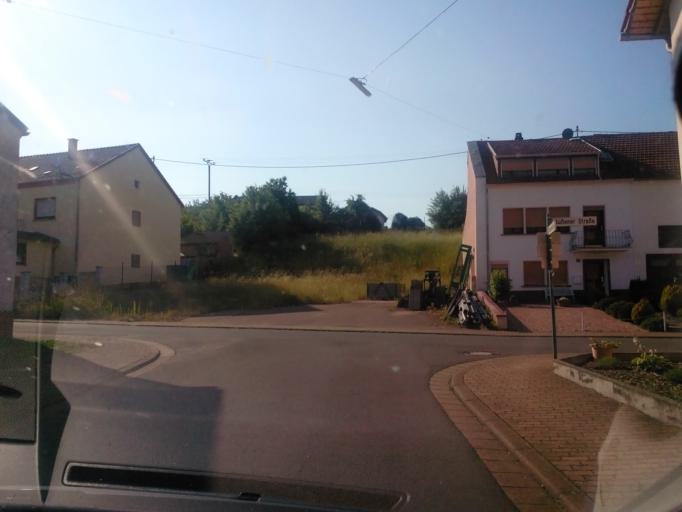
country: DE
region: Saarland
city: Nalbach
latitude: 49.4165
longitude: 6.7676
